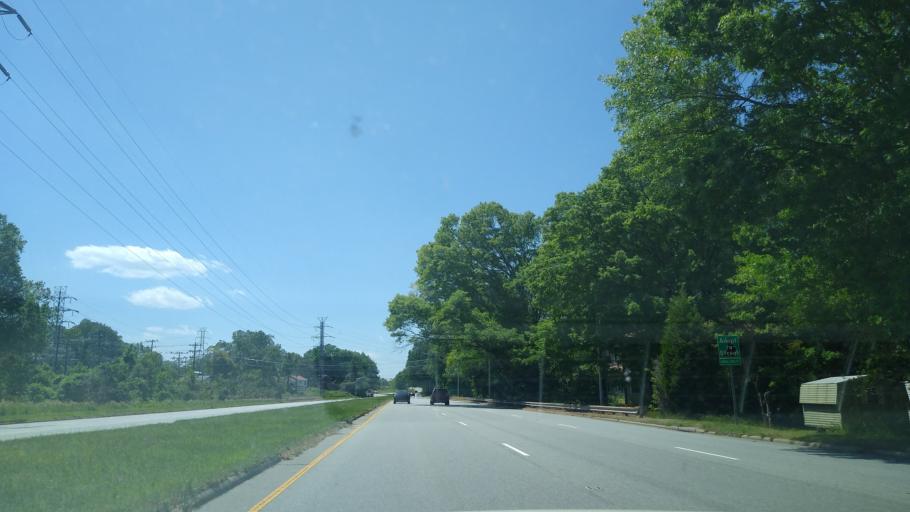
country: US
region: North Carolina
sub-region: Guilford County
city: Greensboro
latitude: 36.0641
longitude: -79.8525
